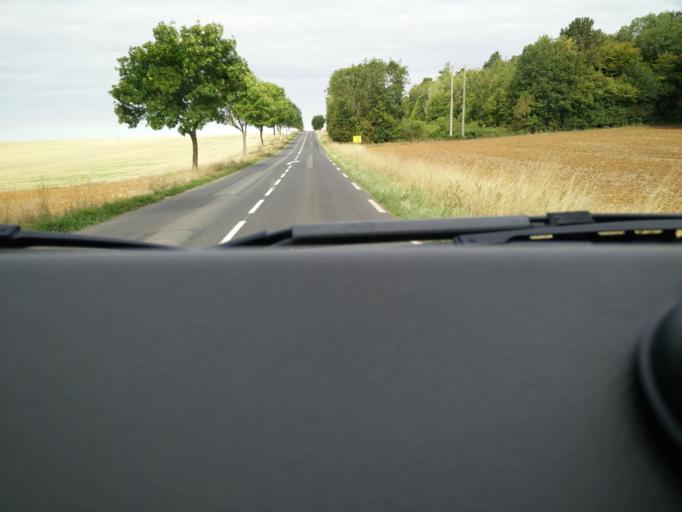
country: FR
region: Lorraine
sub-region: Departement de Meurthe-et-Moselle
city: Montauville
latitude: 48.8956
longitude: 5.9744
